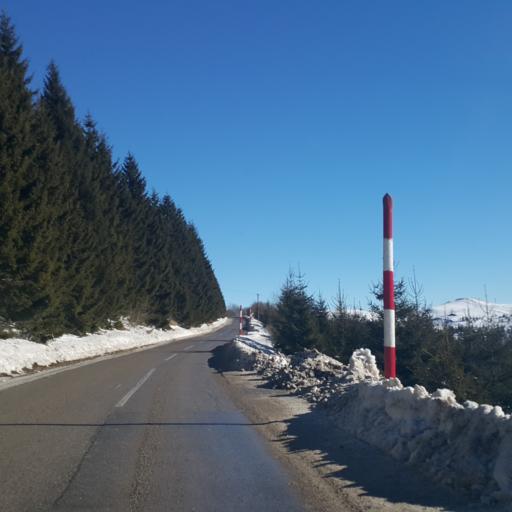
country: XK
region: Mitrovica
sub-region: Komuna e Leposaviqit
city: Leposaviq
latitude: 43.3234
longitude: 20.8452
